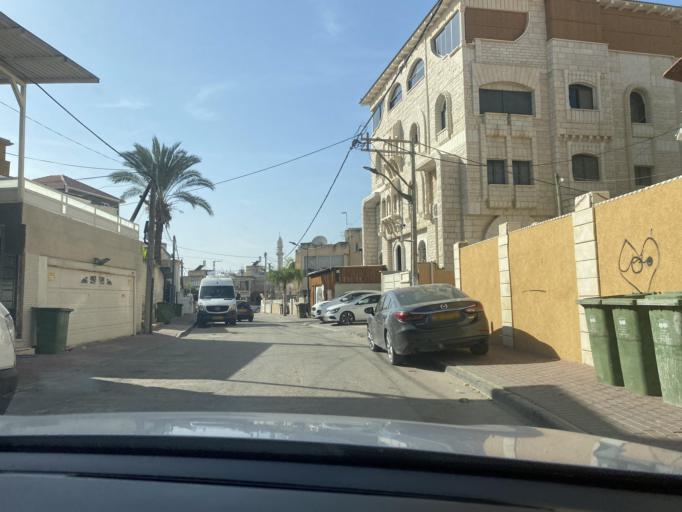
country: IL
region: Central District
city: Kafr Qasim
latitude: 32.1319
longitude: 34.9714
